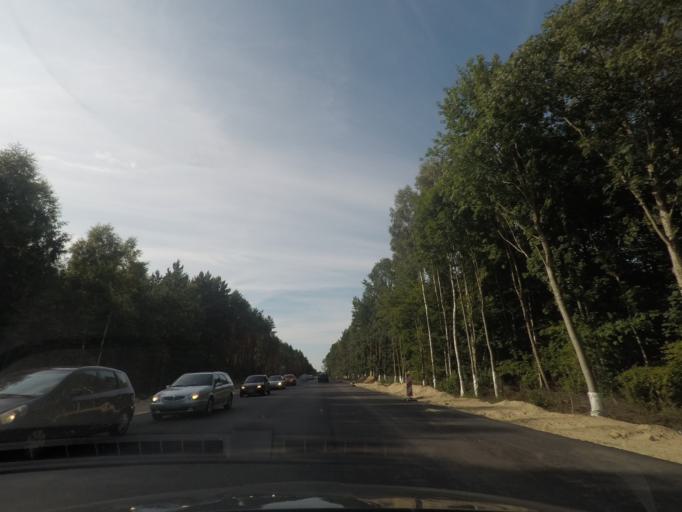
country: PL
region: Pomeranian Voivodeship
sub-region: Powiat leborski
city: Leba
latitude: 54.7147
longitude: 17.5772
